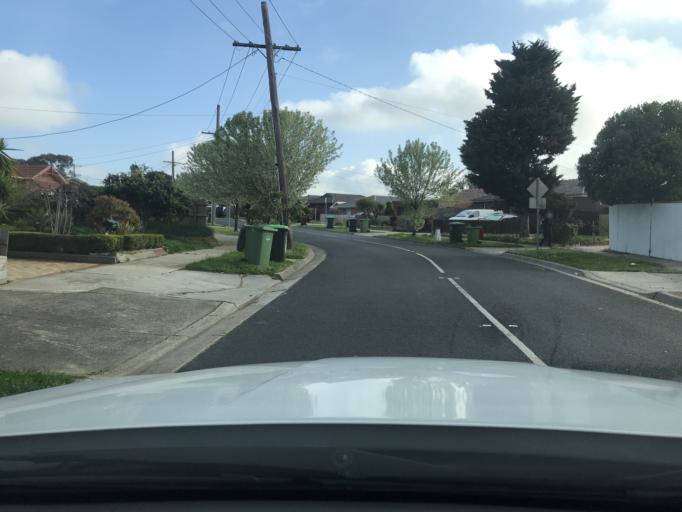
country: AU
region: Victoria
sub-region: Hume
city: Craigieburn
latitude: -37.6011
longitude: 144.9380
